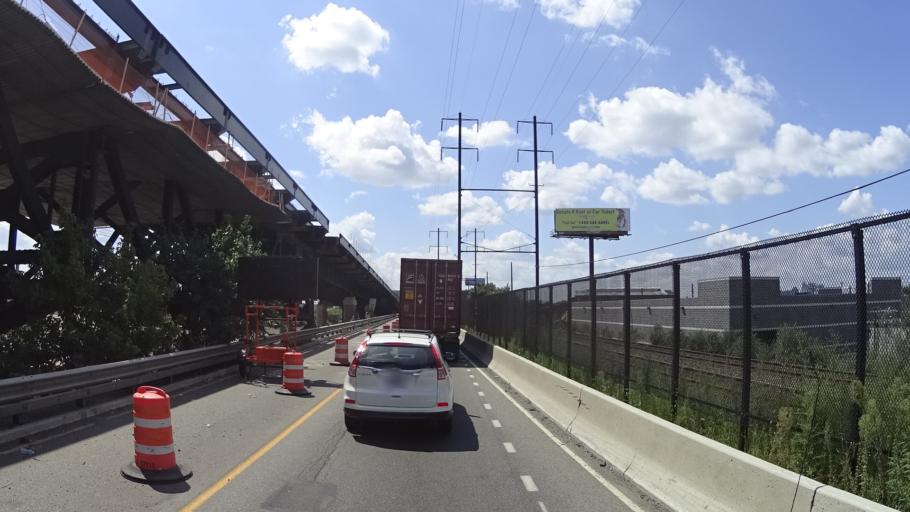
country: US
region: New Jersey
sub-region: Hudson County
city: Harrison
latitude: 40.7342
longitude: -74.1263
